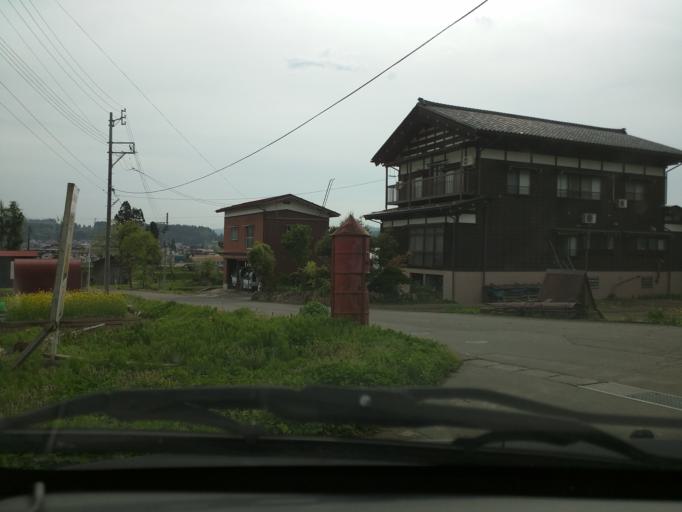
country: JP
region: Niigata
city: Ojiya
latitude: 37.2492
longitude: 138.9339
